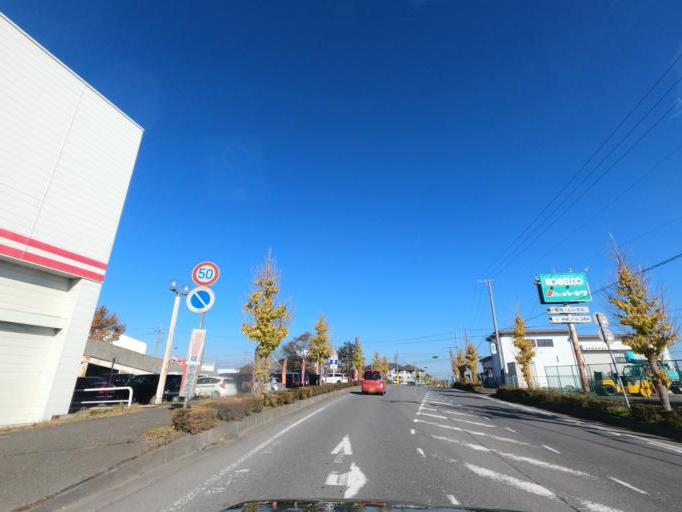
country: JP
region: Ibaraki
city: Mitsukaido
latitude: 35.9881
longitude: 139.9780
